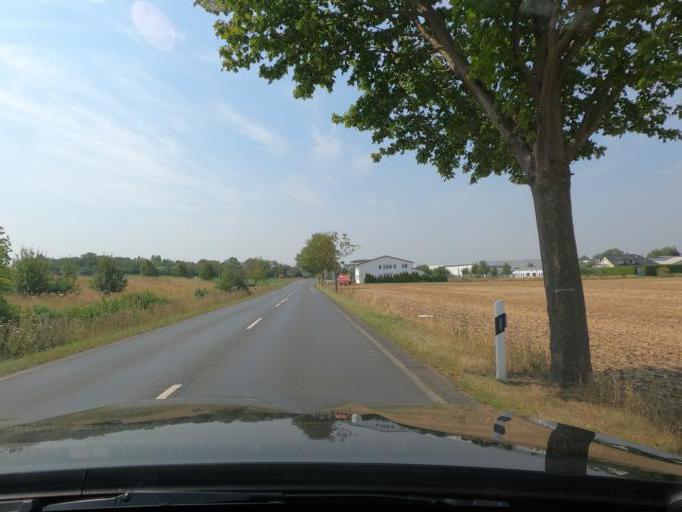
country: DE
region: Lower Saxony
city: Sarstedt
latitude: 52.2757
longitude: 9.8583
